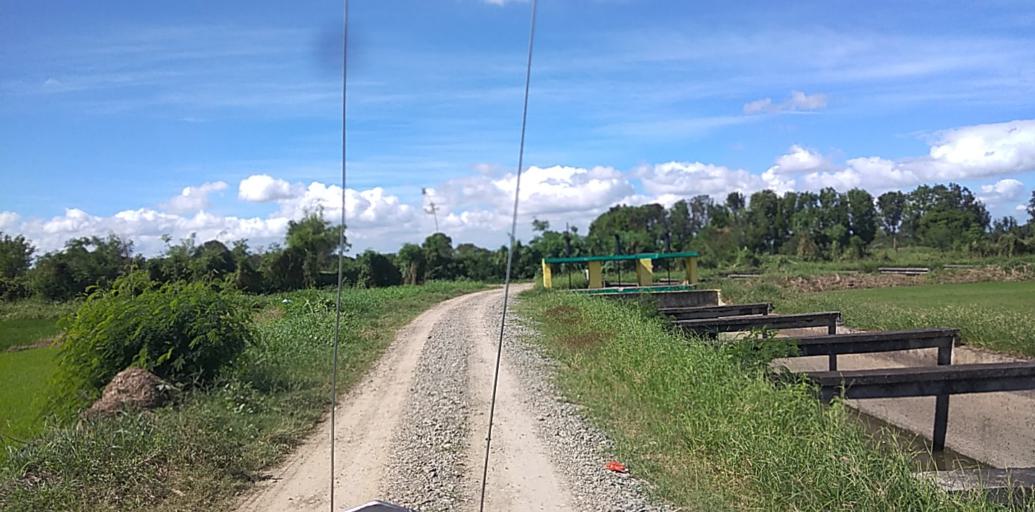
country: PH
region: Central Luzon
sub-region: Province of Pampanga
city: Candating
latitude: 15.1281
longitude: 120.7988
